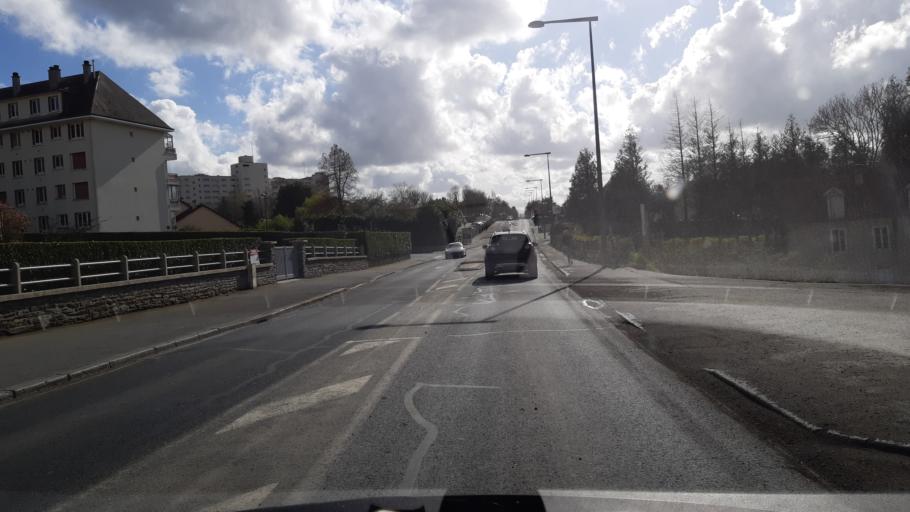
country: FR
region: Lower Normandy
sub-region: Departement de la Manche
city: Agneaux
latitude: 49.1092
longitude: -1.1054
